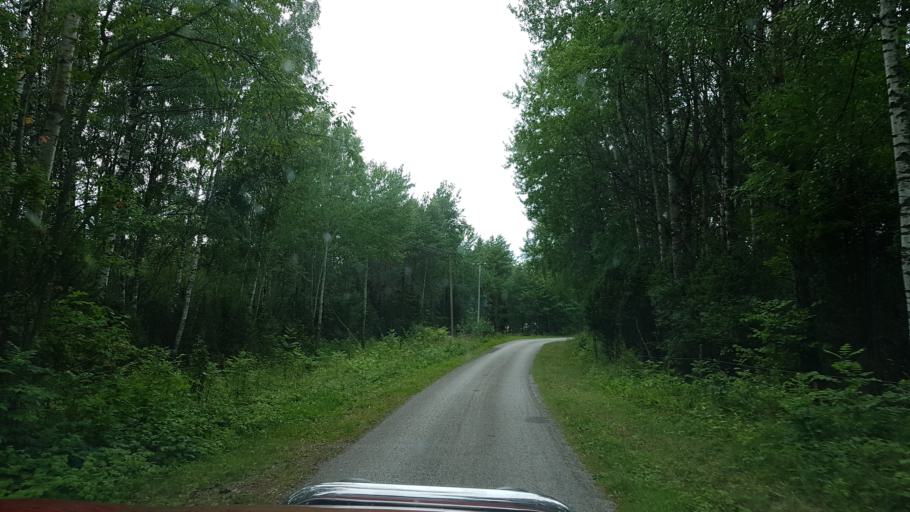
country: EE
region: Laeaene
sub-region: Ridala Parish
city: Uuemoisa
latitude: 58.9989
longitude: 23.6434
